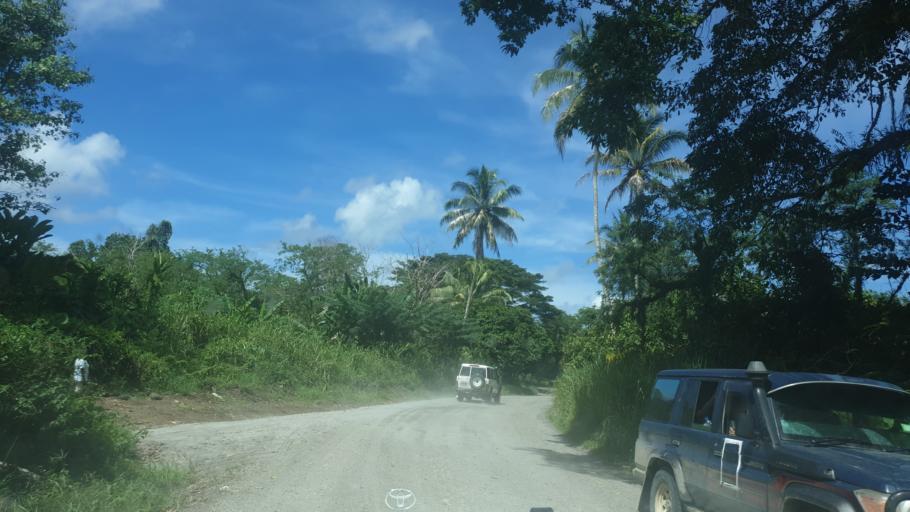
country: PG
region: Bougainville
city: Panguna
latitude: -6.7377
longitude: 155.6691
